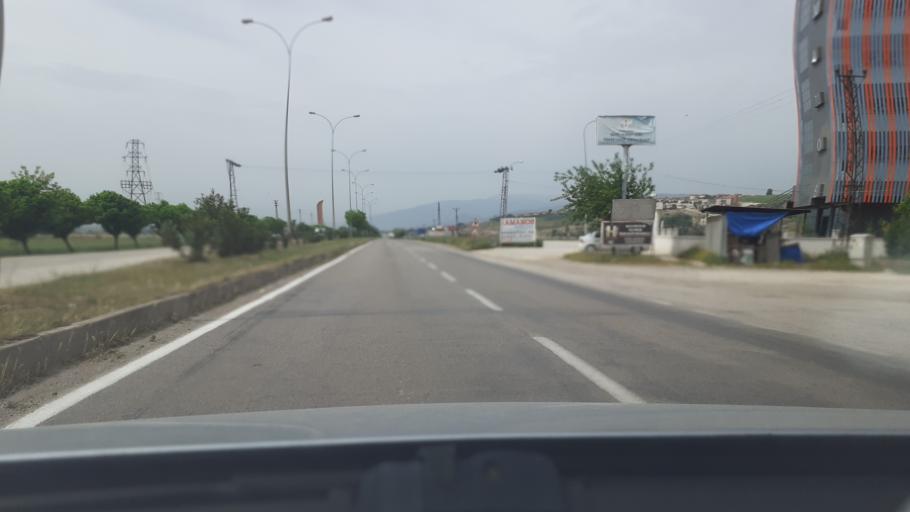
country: TR
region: Hatay
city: Kirikhan
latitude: 36.4793
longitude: 36.3554
